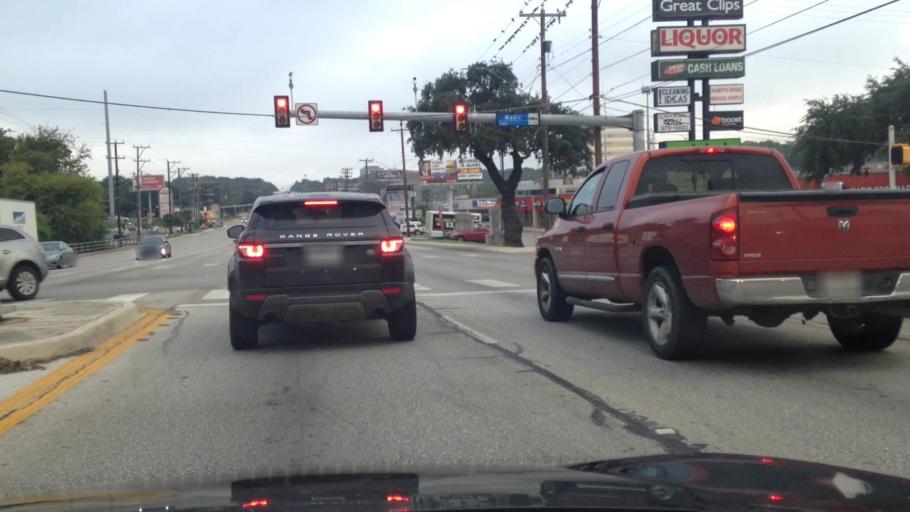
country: US
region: Texas
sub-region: Bexar County
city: Balcones Heights
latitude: 29.5007
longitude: -98.5585
